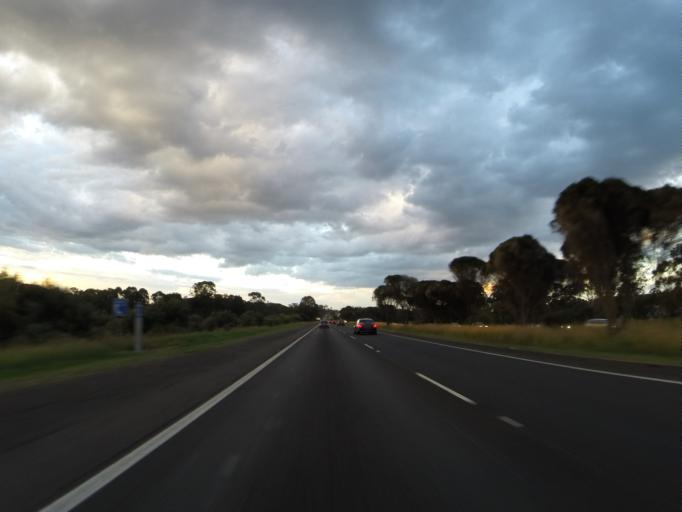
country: AU
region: New South Wales
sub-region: Campbelltown Municipality
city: Glen Alpine
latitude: -34.1020
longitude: 150.7632
